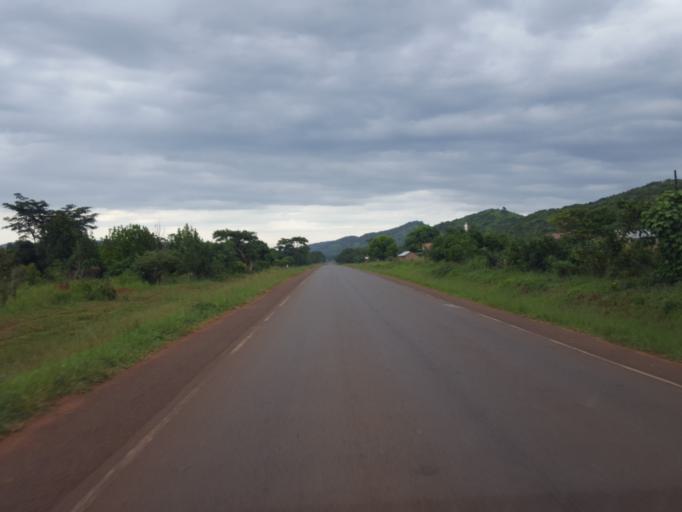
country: UG
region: Central Region
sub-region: Kiboga District
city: Kiboga
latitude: 0.8568
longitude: 31.8663
